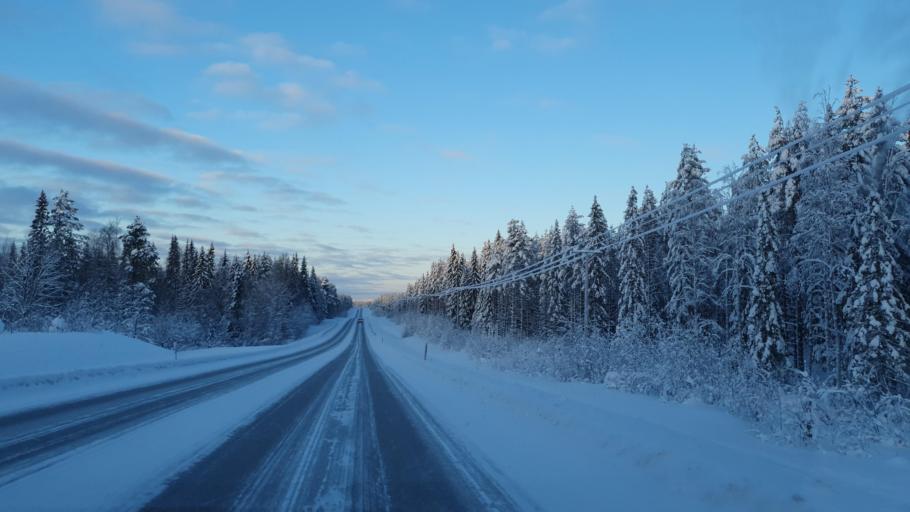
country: FI
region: Kainuu
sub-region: Kajaani
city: Ristijaervi
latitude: 64.3472
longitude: 28.0530
